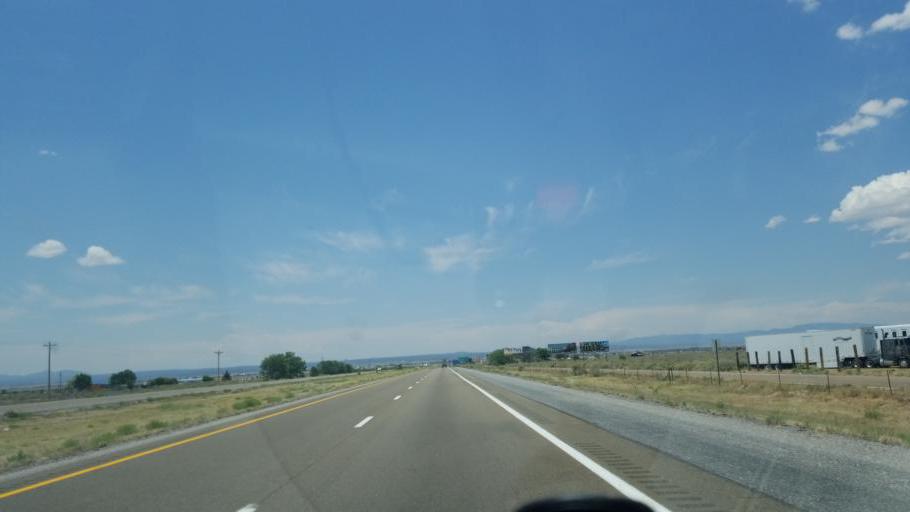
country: US
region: New Mexico
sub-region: Torrance County
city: Moriarty
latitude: 35.0049
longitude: -105.9725
